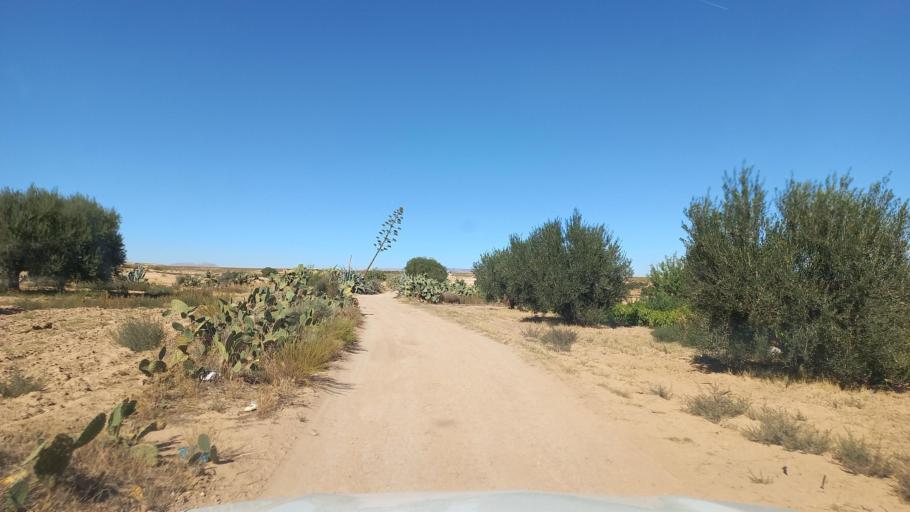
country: TN
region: Al Qasrayn
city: Sbiba
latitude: 35.4044
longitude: 9.0882
